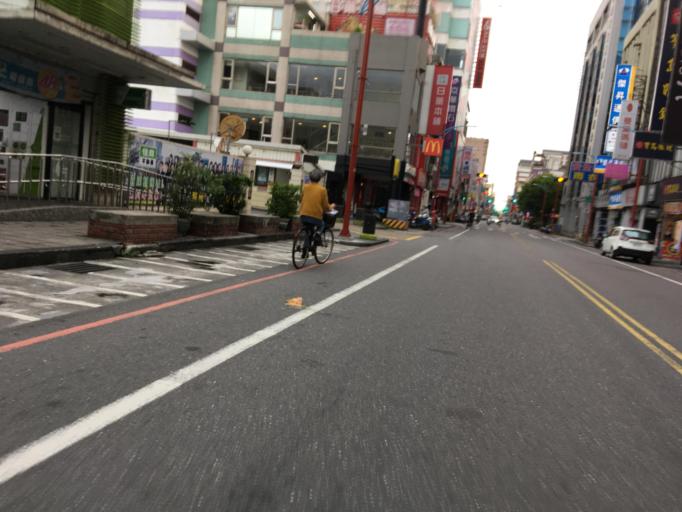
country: TW
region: Taiwan
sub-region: Yilan
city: Yilan
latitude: 24.6776
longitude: 121.7683
